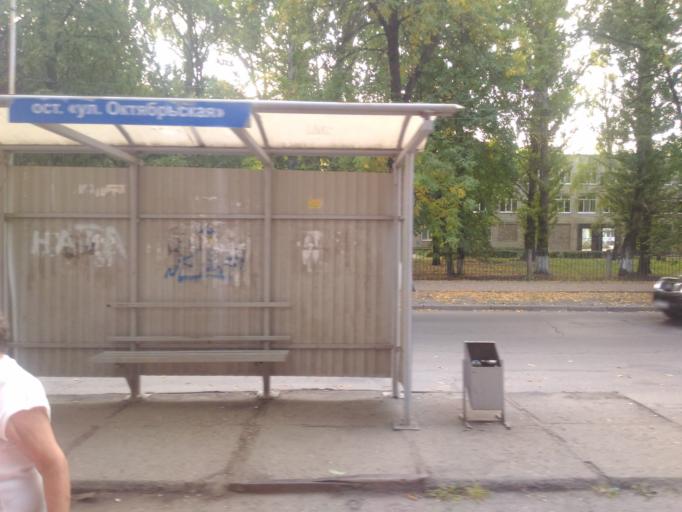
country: RU
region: Ulyanovsk
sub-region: Ulyanovskiy Rayon
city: Ulyanovsk
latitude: 54.2992
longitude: 48.3213
